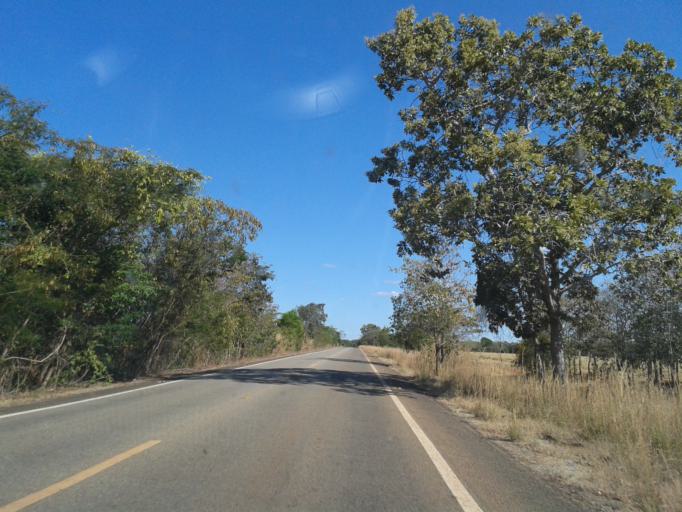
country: BR
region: Goias
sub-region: Mozarlandia
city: Mozarlandia
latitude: -14.2979
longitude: -50.4033
